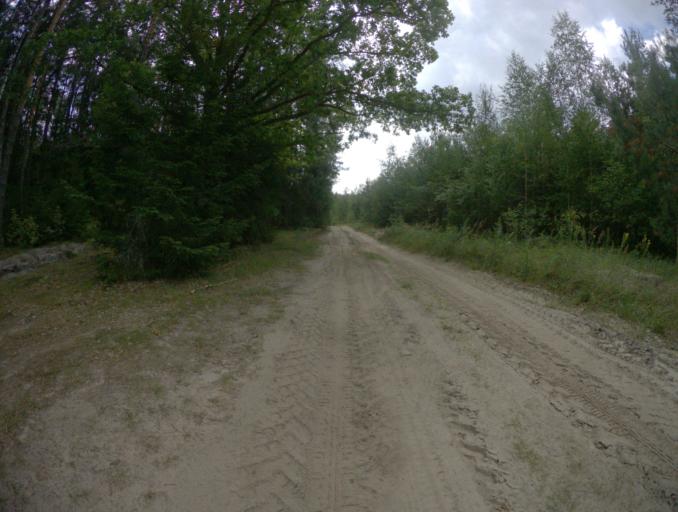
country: RU
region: Vladimir
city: Vorsha
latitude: 55.9642
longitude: 40.1594
